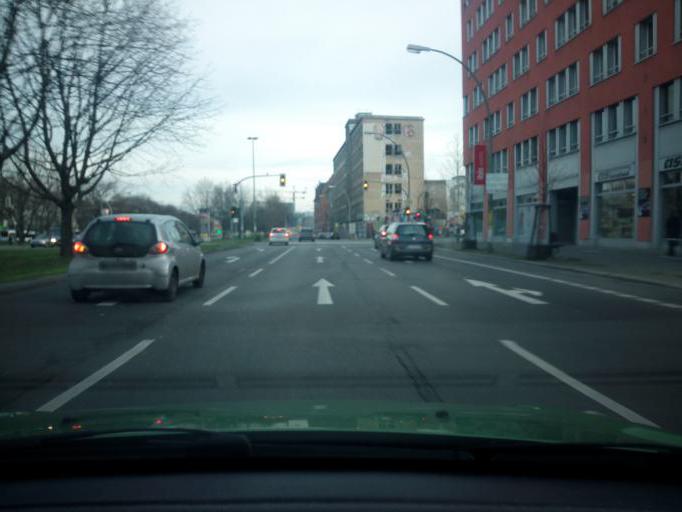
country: DE
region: Berlin
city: Berlin Treptow
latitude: 52.5106
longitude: 13.4293
